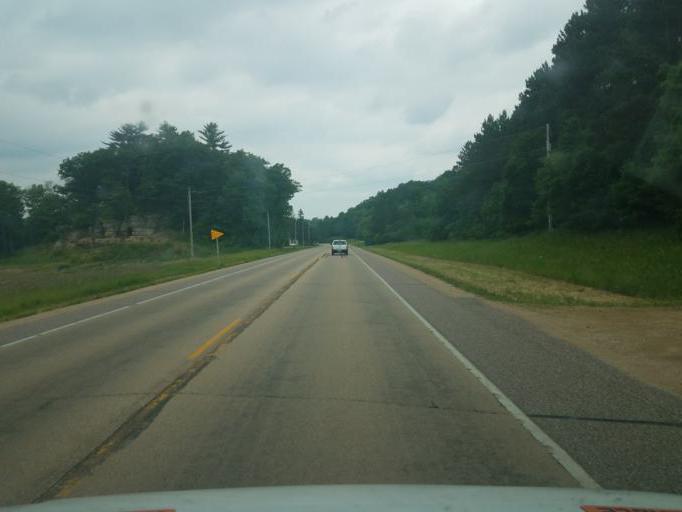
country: US
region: Wisconsin
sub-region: Juneau County
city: Elroy
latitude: 43.6392
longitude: -90.1833
